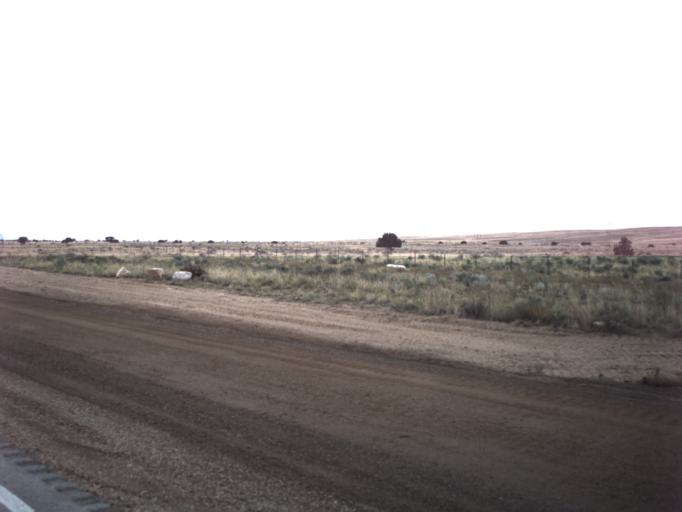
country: US
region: Utah
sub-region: Carbon County
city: East Carbon City
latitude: 39.4319
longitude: -110.4536
